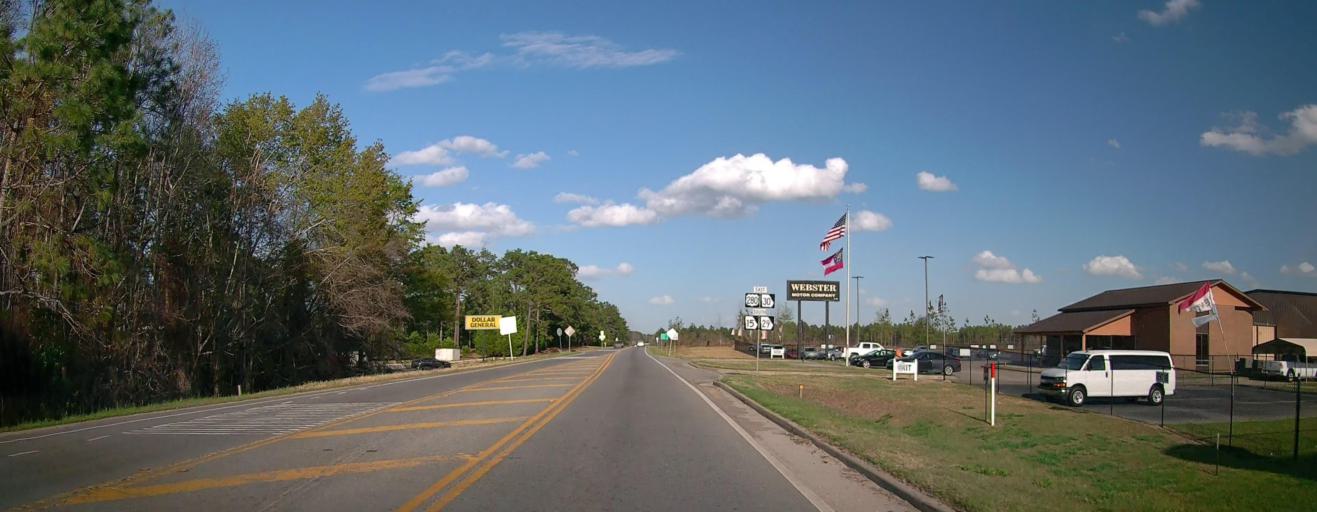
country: US
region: Georgia
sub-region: Toombs County
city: Vidalia
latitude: 32.2116
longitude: -82.4637
